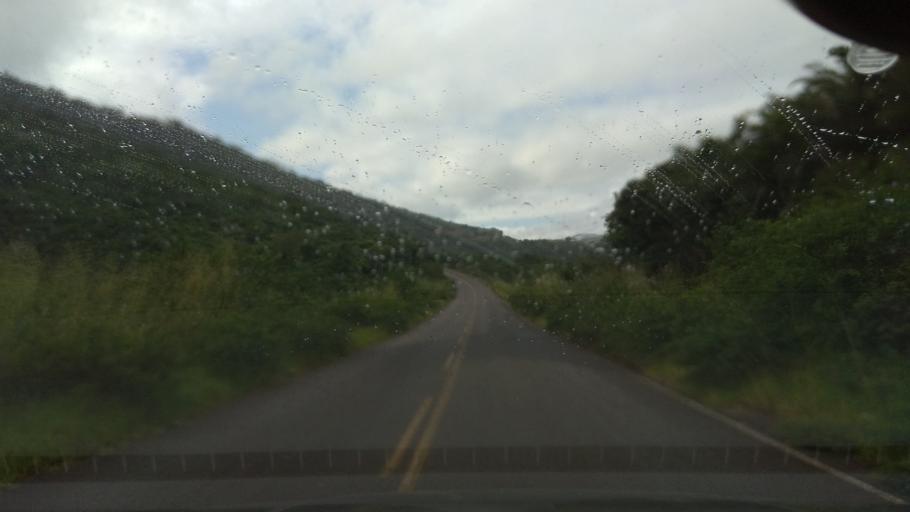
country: BR
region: Bahia
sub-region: Ubaira
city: Ubaira
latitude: -13.2494
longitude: -39.7357
